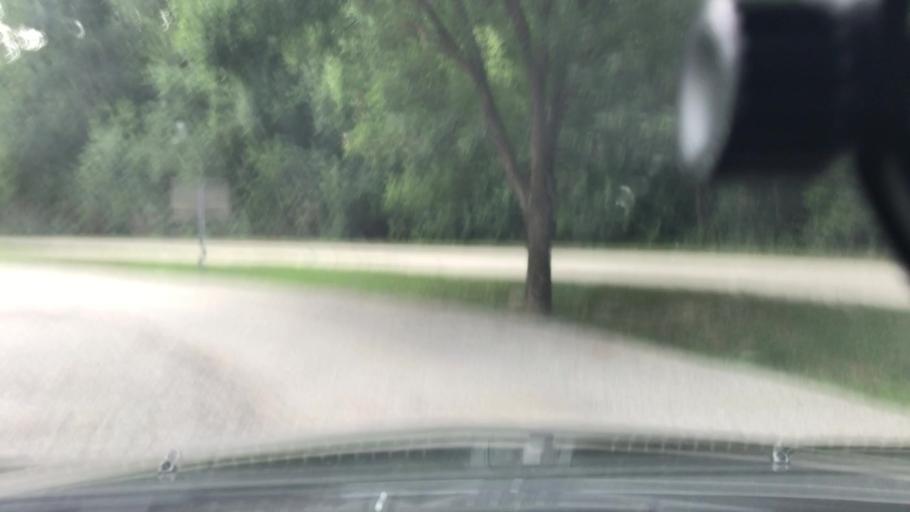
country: US
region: Missouri
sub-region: Saint Charles County
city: Saint Charles
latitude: 38.7452
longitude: -90.5110
